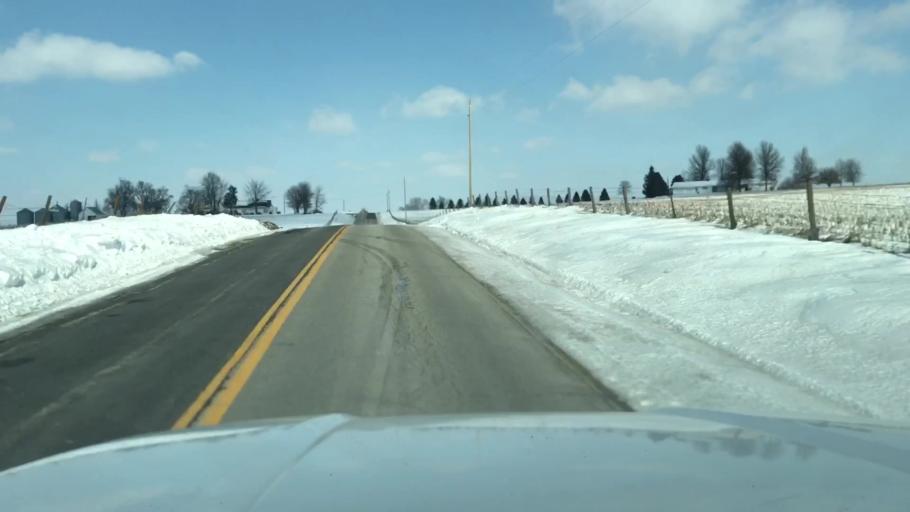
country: US
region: Missouri
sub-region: Nodaway County
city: Maryville
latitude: 40.3593
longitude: -94.7220
